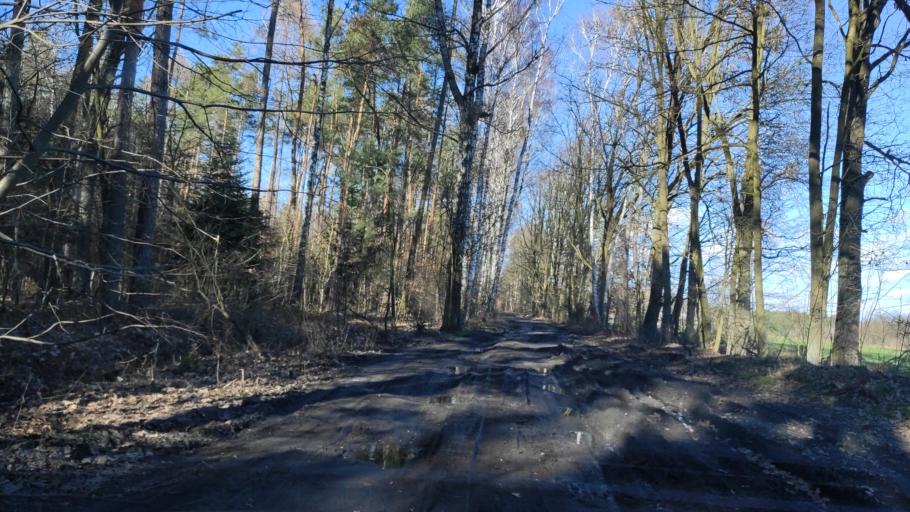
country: PL
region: Masovian Voivodeship
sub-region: Powiat radomski
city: Jedlnia-Letnisko
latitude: 51.4585
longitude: 21.3240
